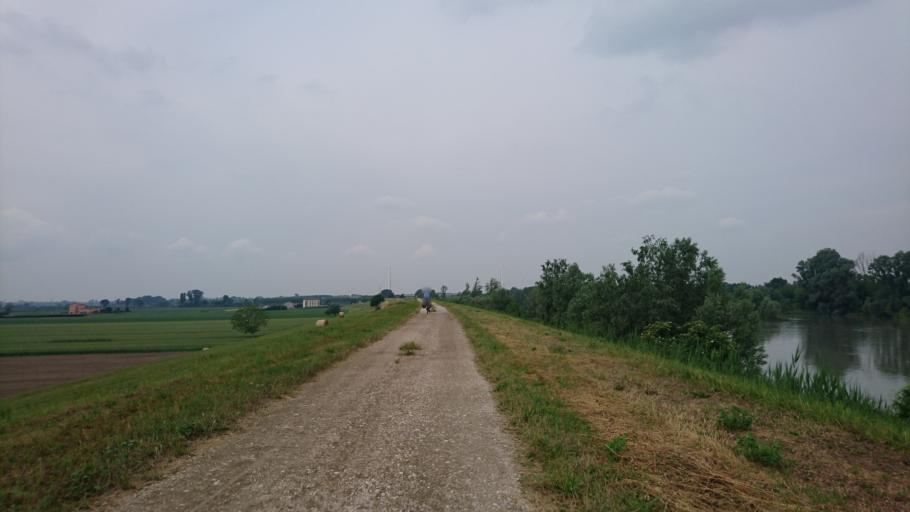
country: IT
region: Veneto
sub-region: Provincia di Padova
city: Piacenza d'Adige
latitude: 45.1196
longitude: 11.5491
